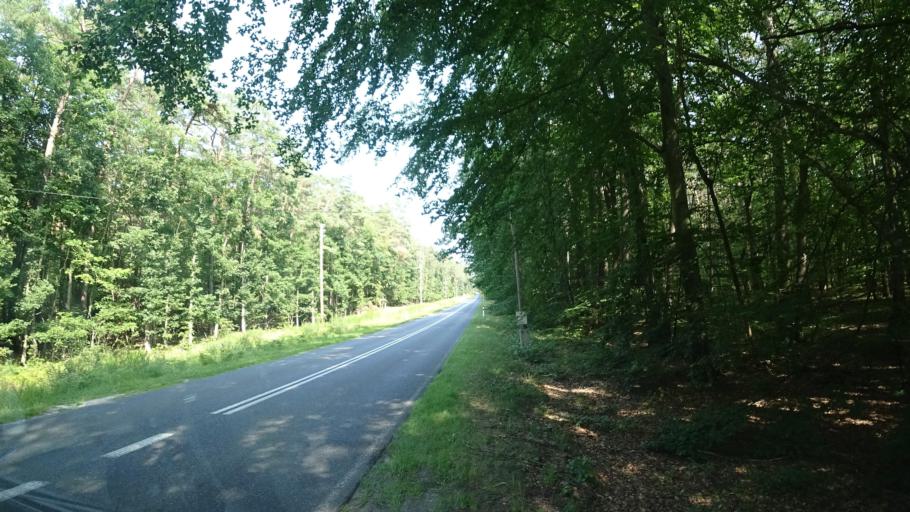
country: PL
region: West Pomeranian Voivodeship
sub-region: Powiat kamienski
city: Miedzyzdroje
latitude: 53.9639
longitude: 14.5432
